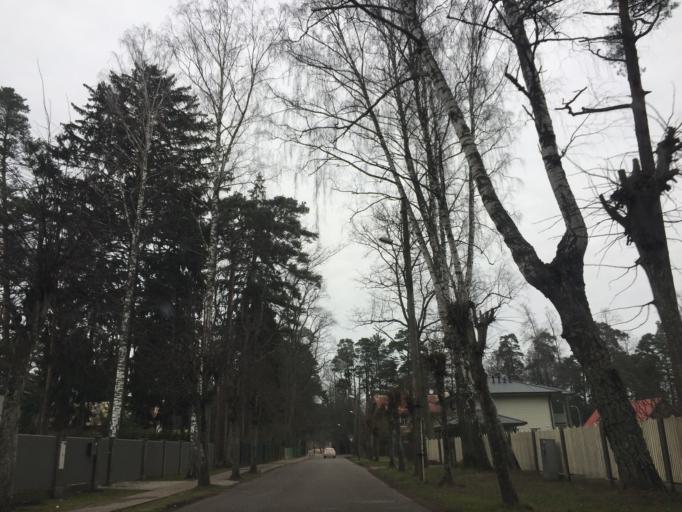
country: LV
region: Jurmala
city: Jurmala
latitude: 56.9623
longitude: 23.7369
